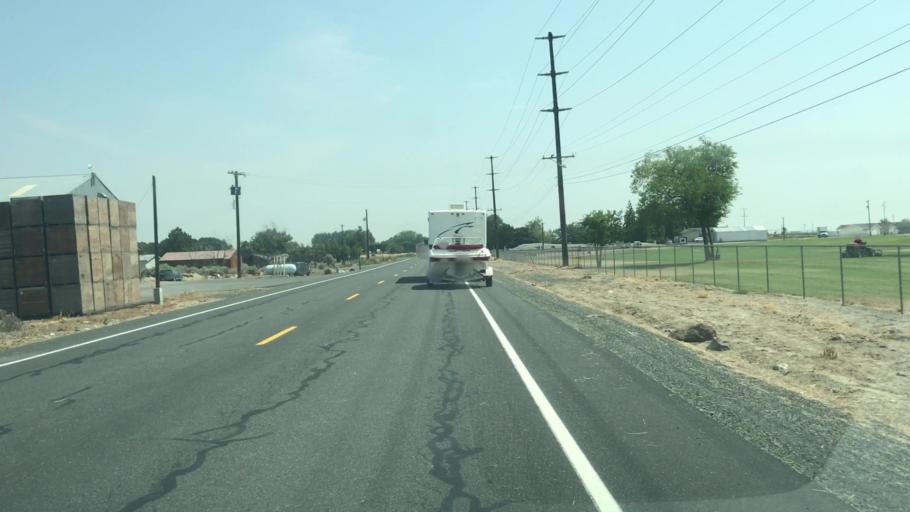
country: US
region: Washington
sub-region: Grant County
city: Quincy
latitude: 47.1613
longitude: -119.8715
